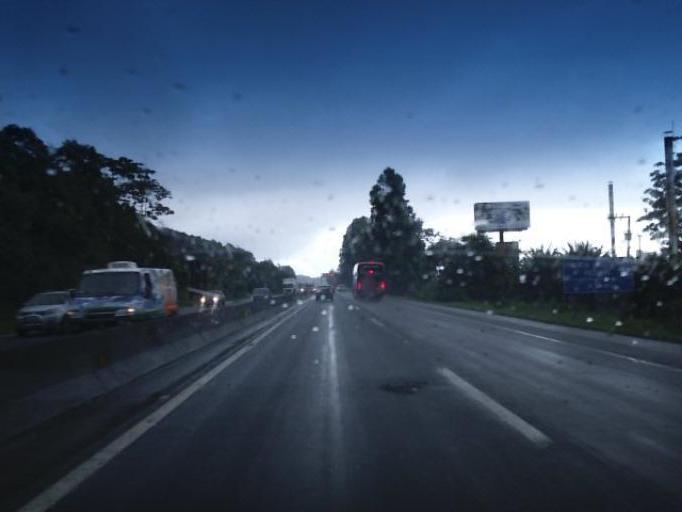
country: BR
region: Santa Catarina
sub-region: Itapema
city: Itapema
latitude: -27.0787
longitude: -48.5997
